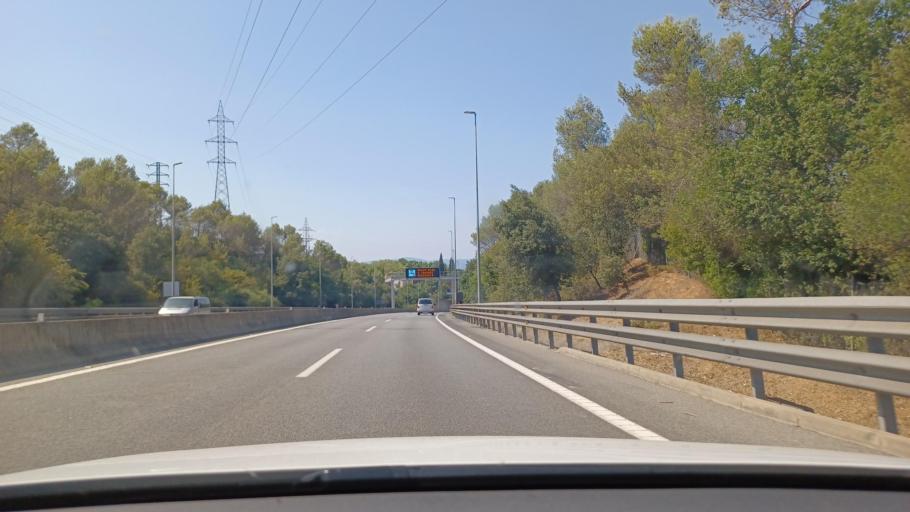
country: ES
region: Catalonia
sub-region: Provincia de Barcelona
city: Sant Cugat del Valles
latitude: 41.4547
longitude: 2.0679
